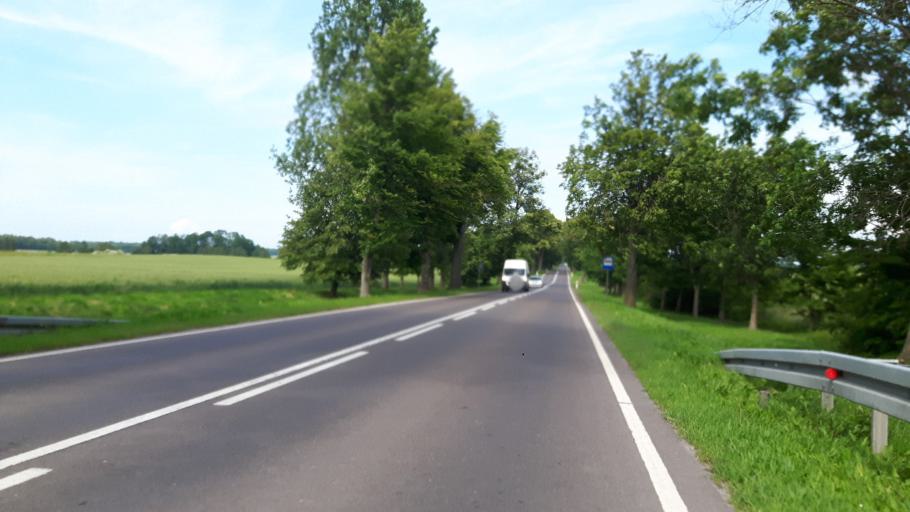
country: PL
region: Warmian-Masurian Voivodeship
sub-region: Powiat braniewski
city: Braniewo
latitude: 54.4110
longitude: 19.8662
